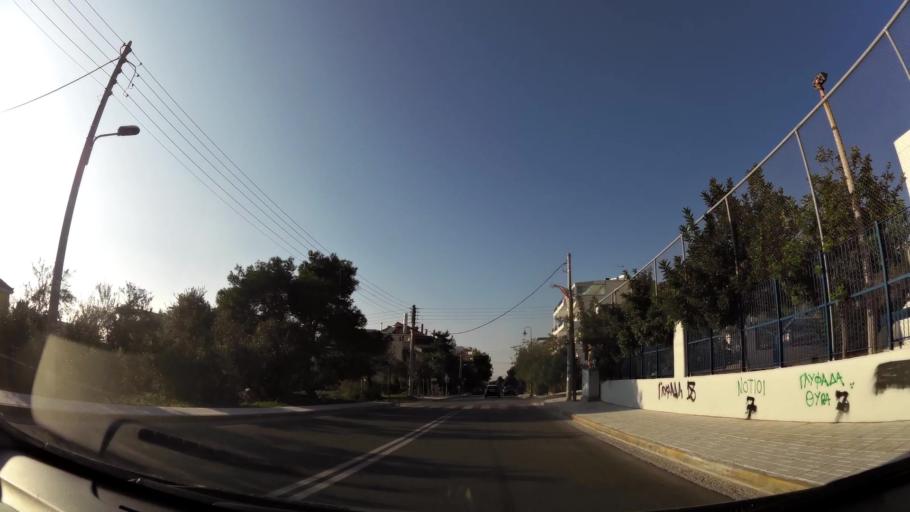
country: GR
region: Attica
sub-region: Nomarchia Athinas
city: Glyfada
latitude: 37.8846
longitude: 23.7737
